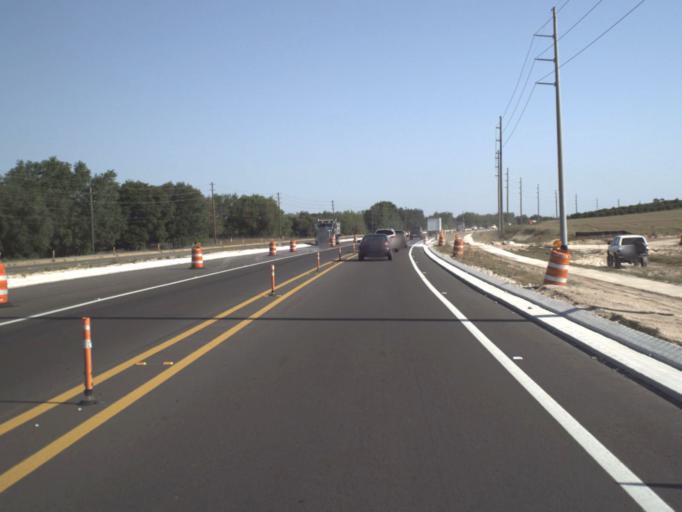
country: US
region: Florida
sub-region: Lake County
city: Clermont
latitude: 28.4617
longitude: -81.7203
